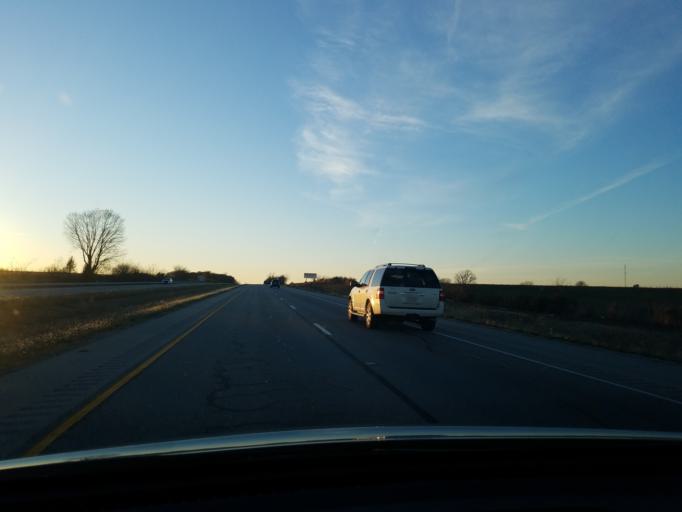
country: US
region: Indiana
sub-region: Posey County
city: Poseyville
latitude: 38.1842
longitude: -87.7942
